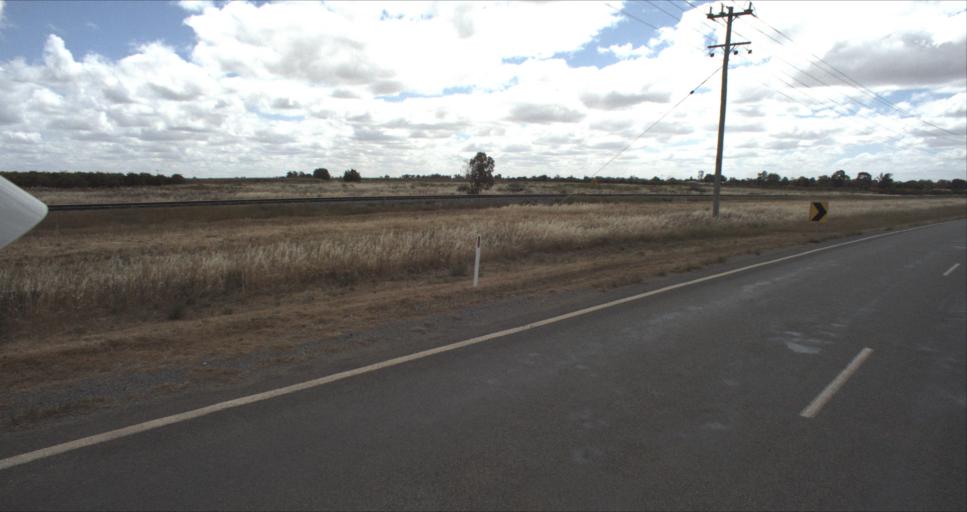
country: AU
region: New South Wales
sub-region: Leeton
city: Leeton
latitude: -34.5760
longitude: 146.3953
